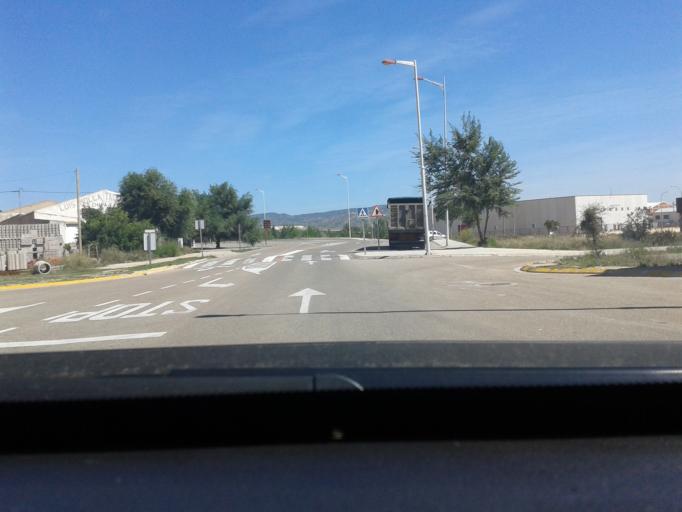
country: ES
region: Castille-La Mancha
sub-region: Provincia de Albacete
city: Caudete
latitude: 38.7087
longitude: -0.9806
